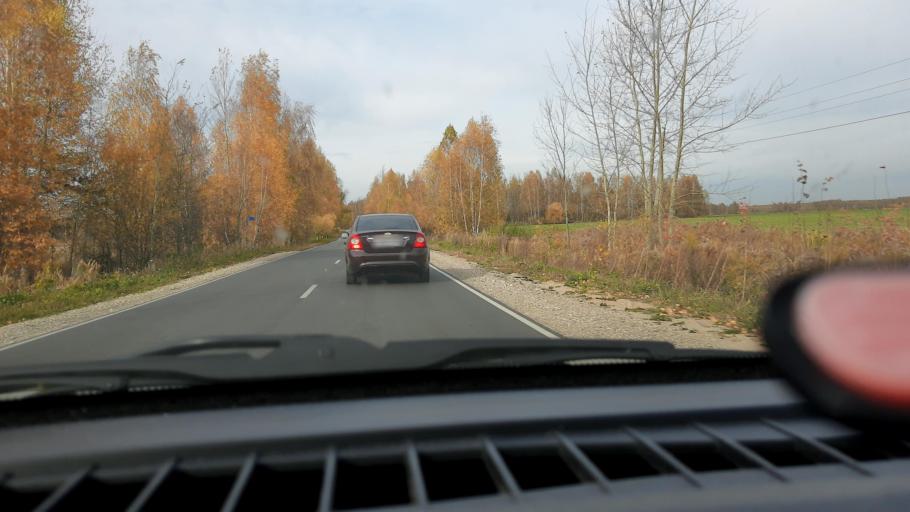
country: RU
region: Nizjnij Novgorod
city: Neklyudovo
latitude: 56.4611
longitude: 43.9020
